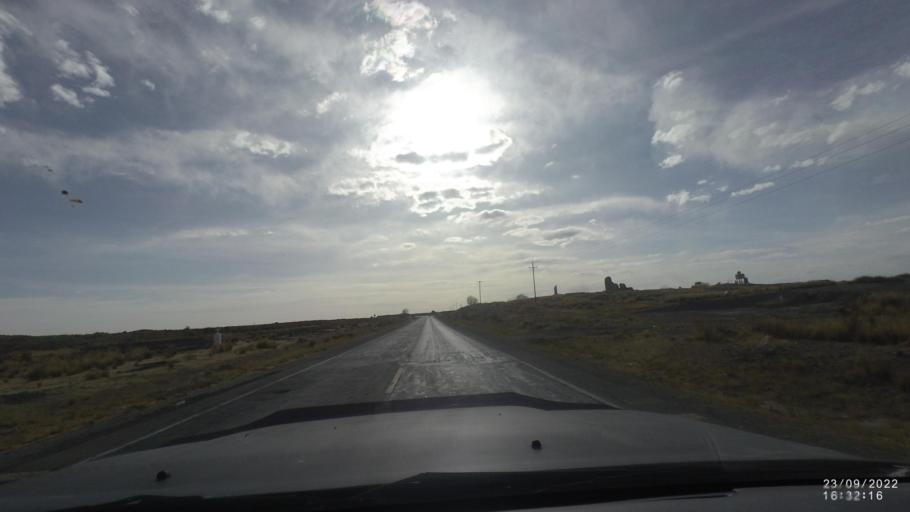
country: BO
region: Oruro
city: Machacamarca
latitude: -18.1639
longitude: -67.0033
